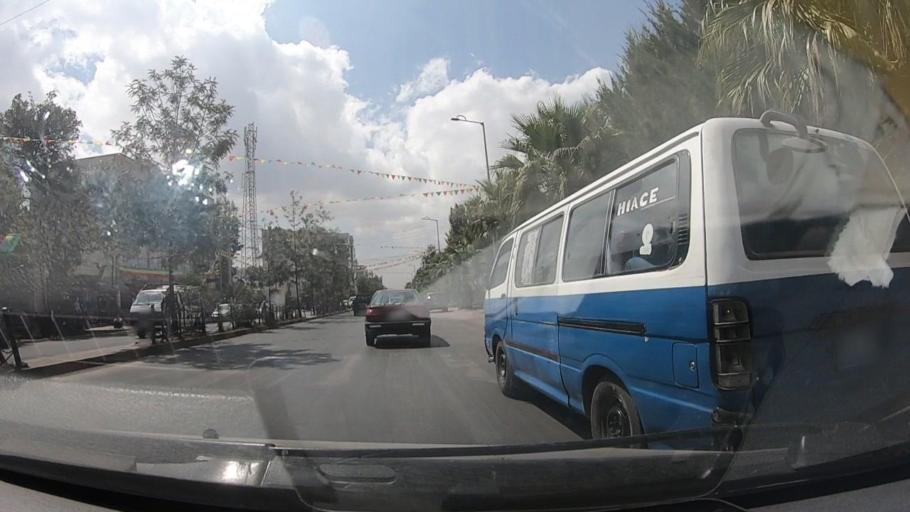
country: ET
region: Adis Abeba
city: Addis Ababa
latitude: 8.9919
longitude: 38.7260
